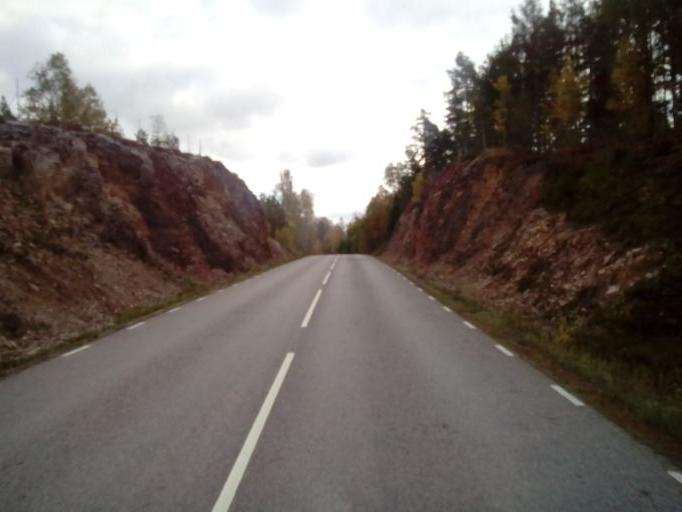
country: SE
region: Kalmar
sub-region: Vasterviks Kommun
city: Gamleby
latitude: 57.8885
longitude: 16.3270
